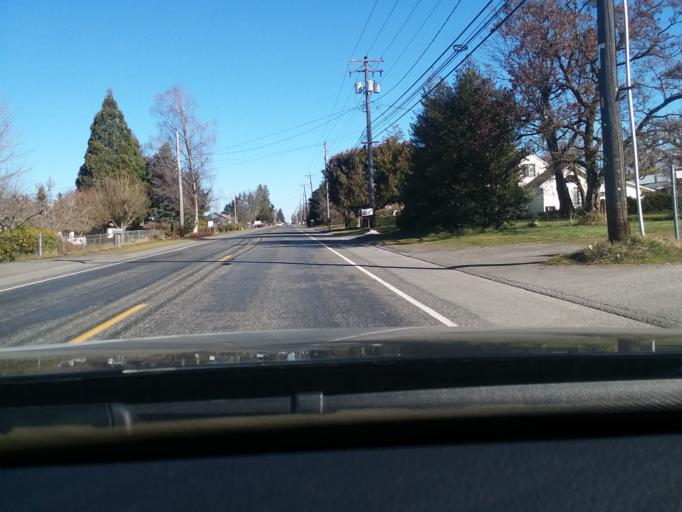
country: US
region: Washington
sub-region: Pierce County
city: Midland
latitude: 47.1656
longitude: -122.3890
